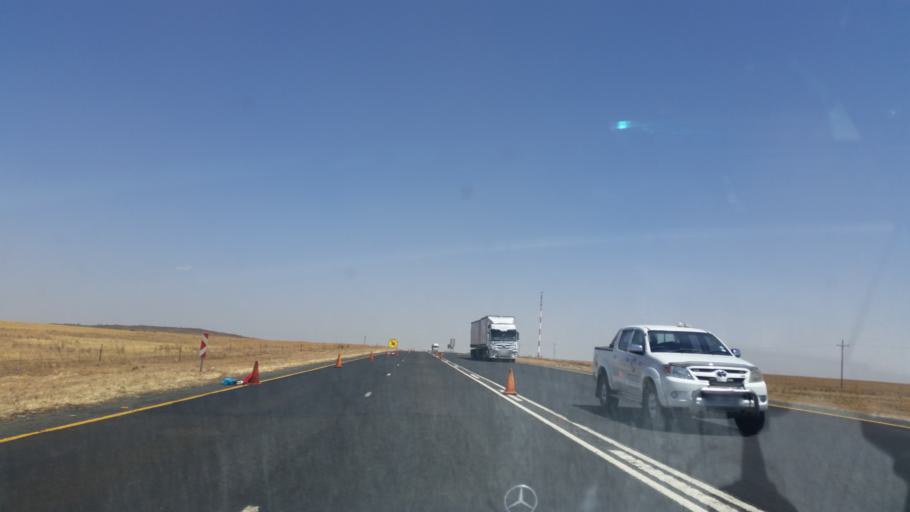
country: ZA
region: Orange Free State
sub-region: Lejweleputswa District Municipality
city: Brandfort
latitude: -28.8101
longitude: 26.6757
